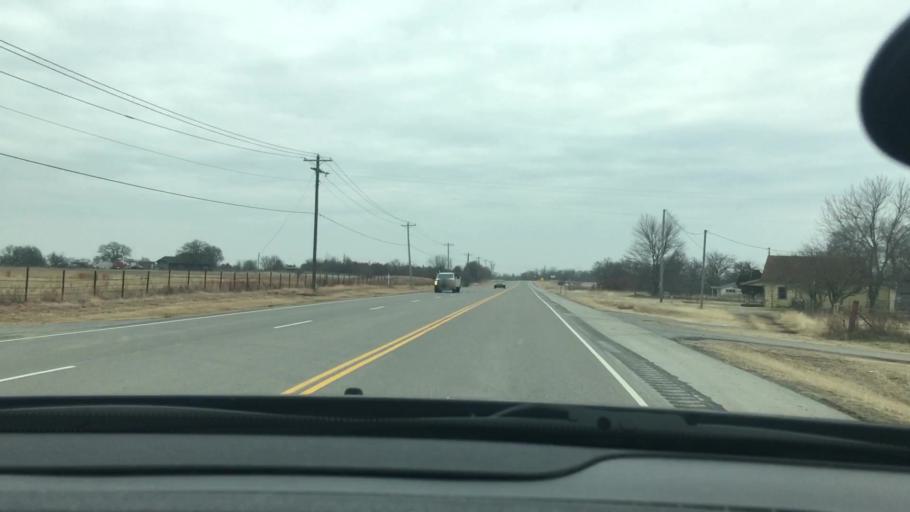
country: US
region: Oklahoma
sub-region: Carter County
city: Healdton
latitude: 34.3970
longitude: -97.5041
